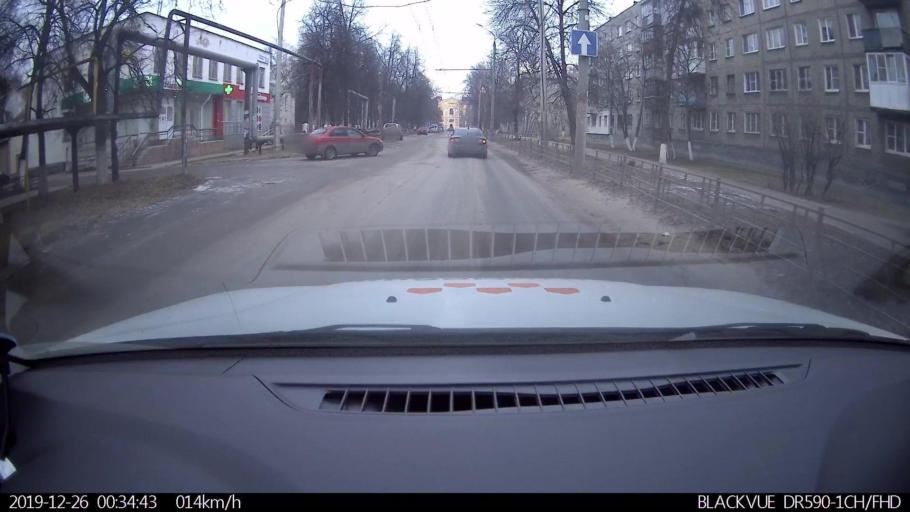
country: RU
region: Nizjnij Novgorod
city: Nizhniy Novgorod
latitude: 56.2903
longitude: 43.9156
